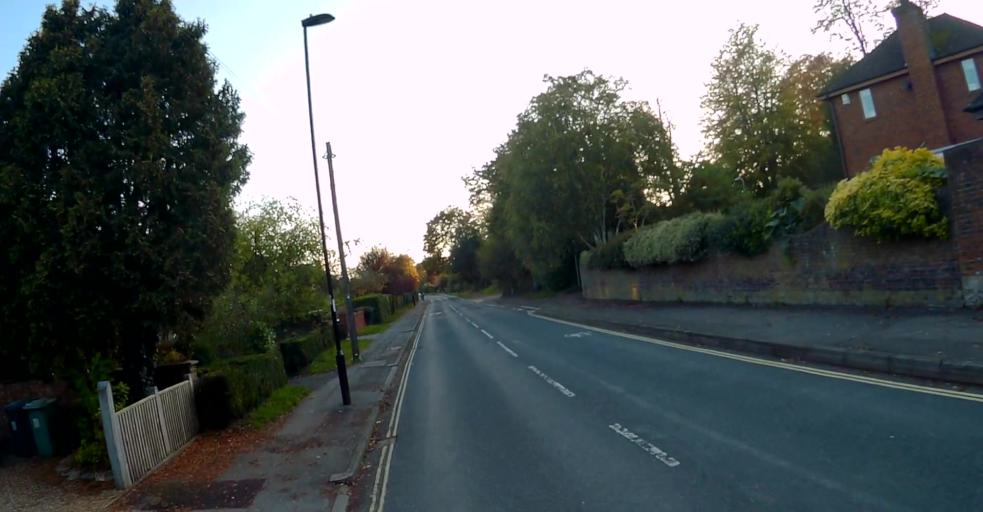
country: GB
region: England
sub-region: Hampshire
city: Basingstoke
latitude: 51.2542
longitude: -1.0866
